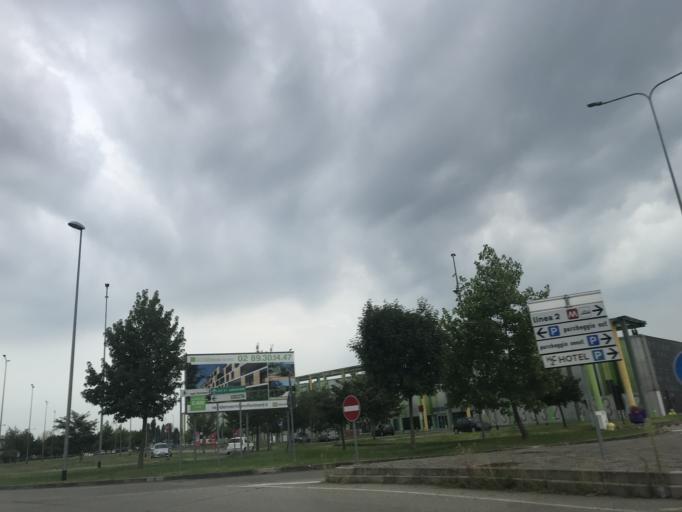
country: IT
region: Lombardy
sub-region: Citta metropolitana di Milano
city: Rozzano
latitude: 45.4085
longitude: 9.1550
